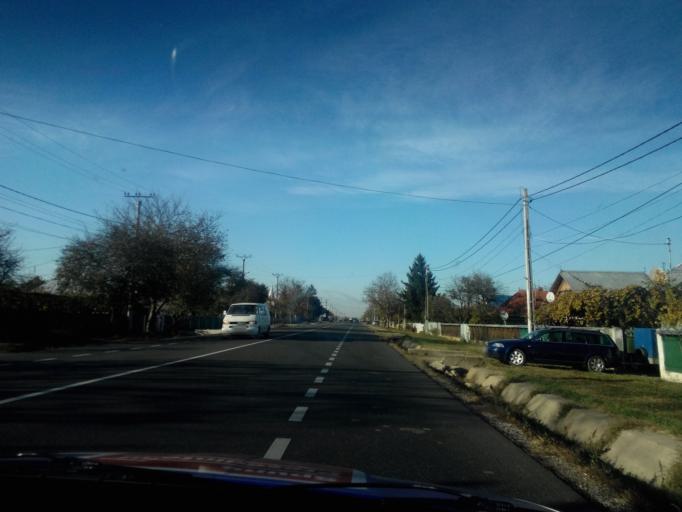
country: RO
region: Bacau
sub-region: Comuna Saucesti
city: Saucesti
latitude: 46.6172
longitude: 26.9218
